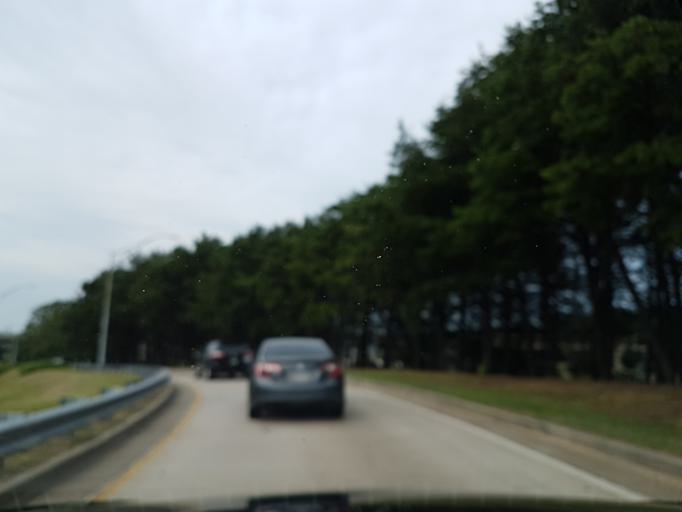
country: US
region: Georgia
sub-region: Fulton County
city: College Park
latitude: 33.6459
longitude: -84.4450
